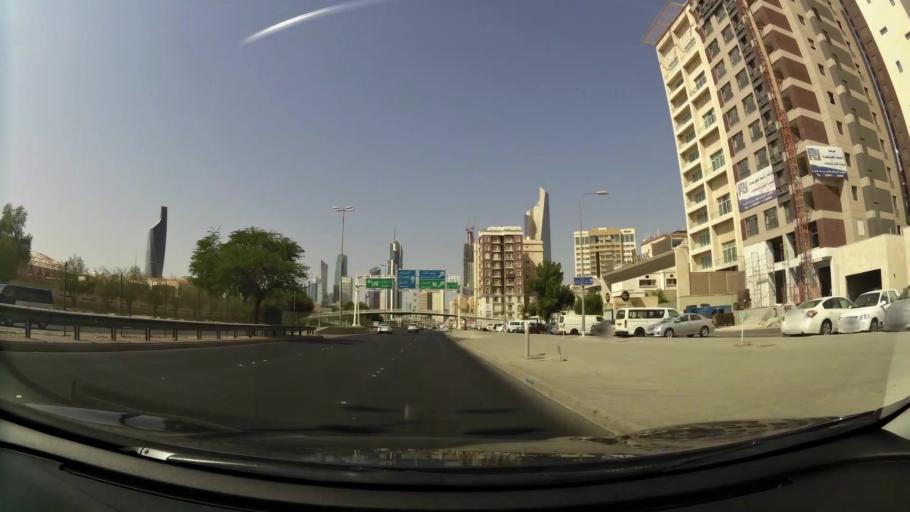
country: KW
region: Al Asimah
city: Ad Dasmah
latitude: 29.3707
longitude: 48.0023
